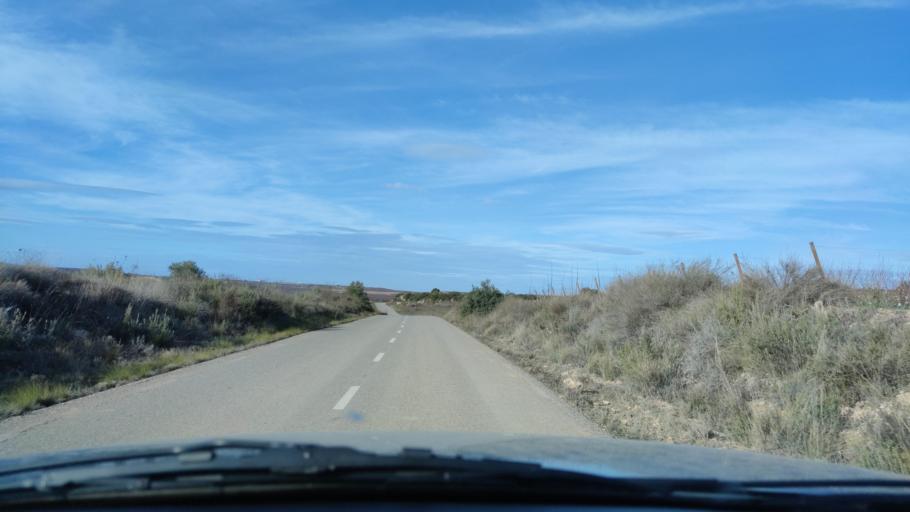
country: ES
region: Catalonia
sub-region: Provincia de Lleida
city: Alcano
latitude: 41.4680
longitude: 0.6477
